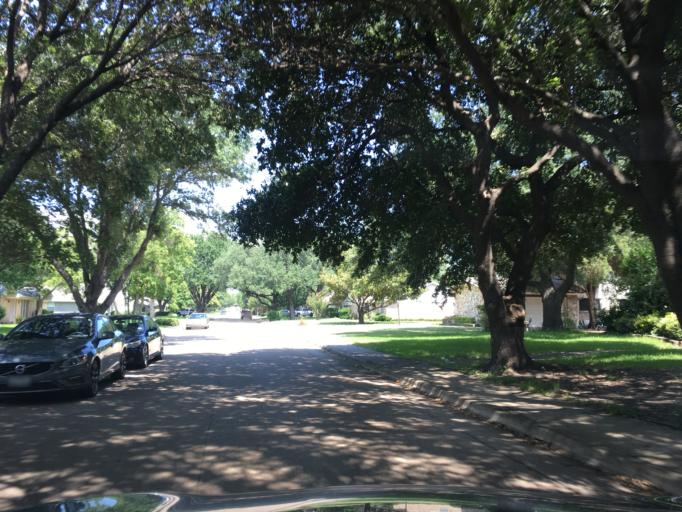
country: US
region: Texas
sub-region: Dallas County
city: Farmers Branch
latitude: 32.9236
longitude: -96.8644
